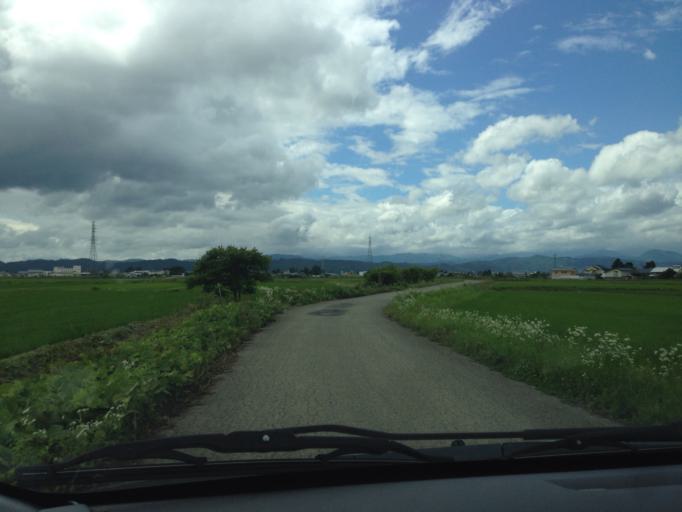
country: JP
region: Fukushima
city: Kitakata
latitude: 37.6299
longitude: 139.9031
